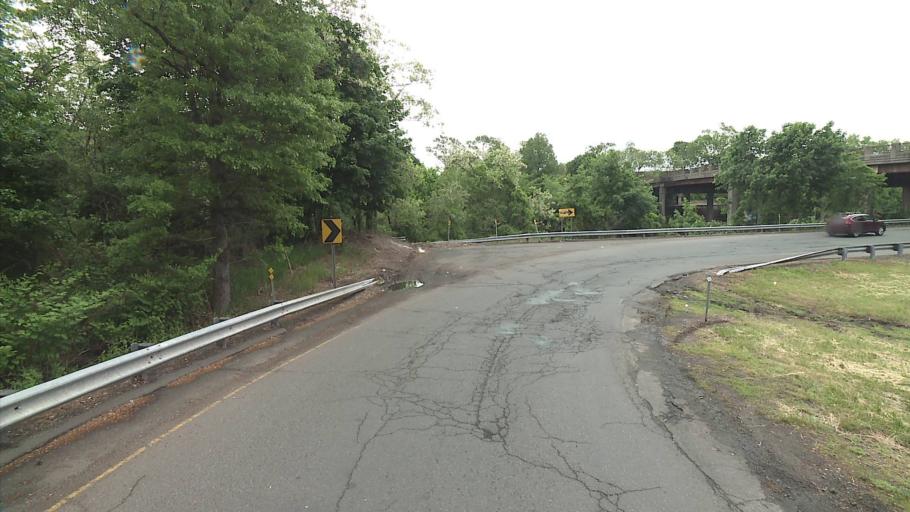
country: US
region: Connecticut
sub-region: New Haven County
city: New Haven
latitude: 41.3196
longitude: -72.9042
